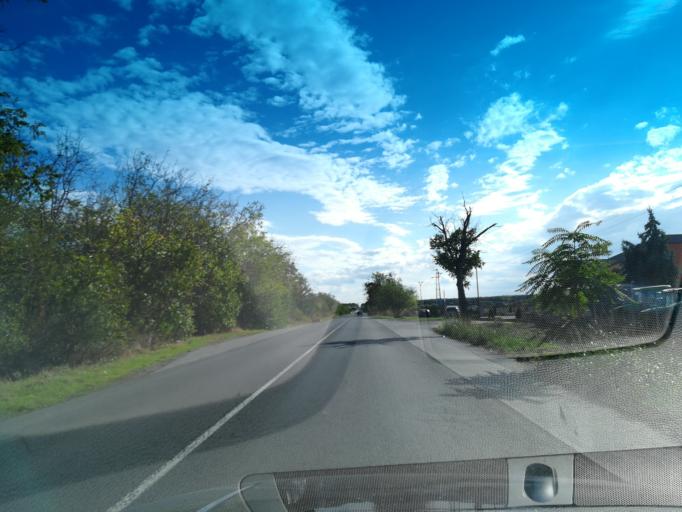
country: BG
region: Stara Zagora
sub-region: Obshtina Stara Zagora
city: Stara Zagora
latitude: 42.3679
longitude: 25.6539
